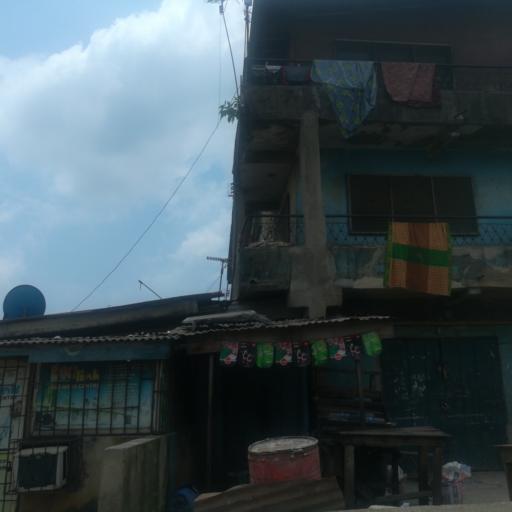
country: NG
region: Lagos
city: Ojota
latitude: 6.5847
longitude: 3.3814
